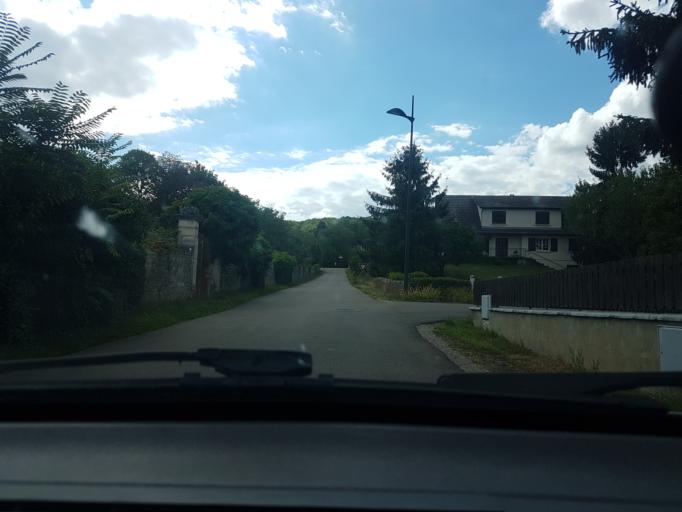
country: FR
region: Bourgogne
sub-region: Departement de Saone-et-Loire
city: Fontaines
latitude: 46.8496
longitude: 4.7564
